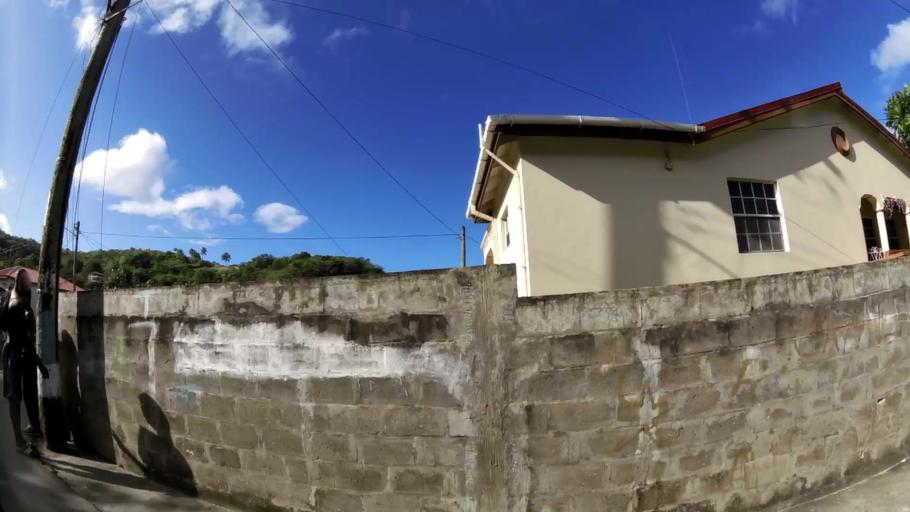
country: LC
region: Anse-la-Raye
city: Canaries
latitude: 13.9051
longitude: -61.0672
